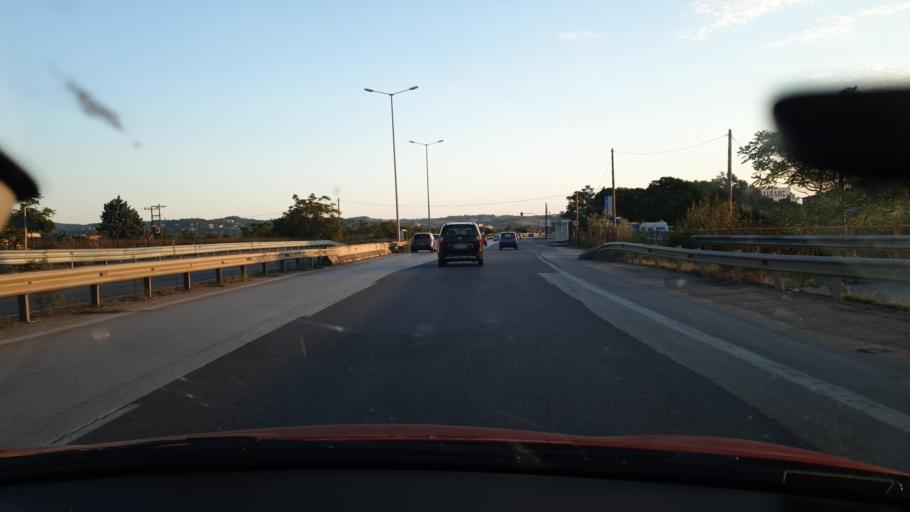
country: GR
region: Central Macedonia
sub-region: Nomos Thessalonikis
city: Neo Rysi
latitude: 40.5195
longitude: 22.9938
